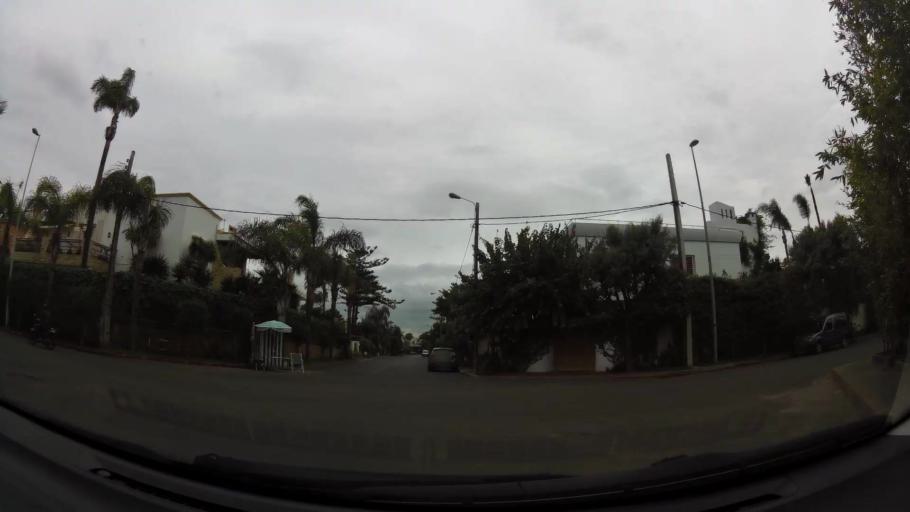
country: MA
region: Grand Casablanca
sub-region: Casablanca
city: Casablanca
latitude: 33.5826
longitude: -7.6560
